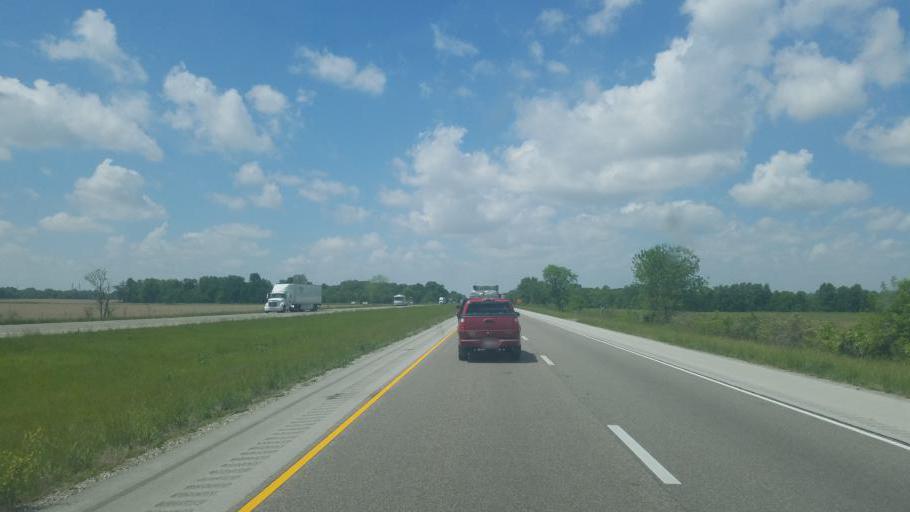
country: US
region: Illinois
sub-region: Cumberland County
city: Toledo
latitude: 39.2259
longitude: -88.2272
